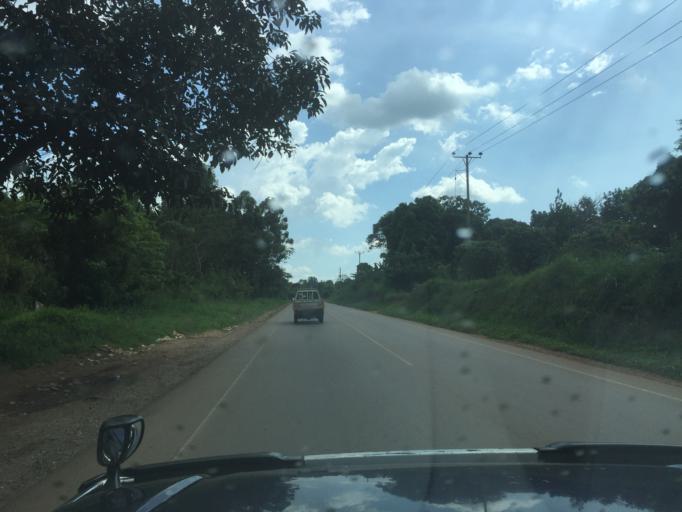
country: UG
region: Central Region
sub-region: Wakiso District
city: Wakiso
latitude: 0.5290
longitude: 32.5274
